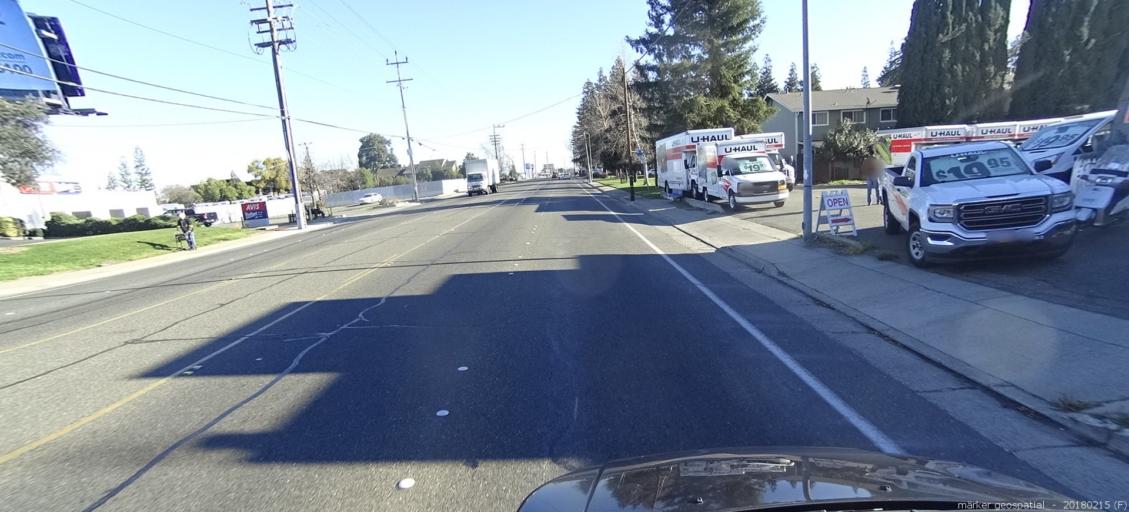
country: US
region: California
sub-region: Sacramento County
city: Foothill Farms
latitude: 38.6760
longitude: -121.3245
